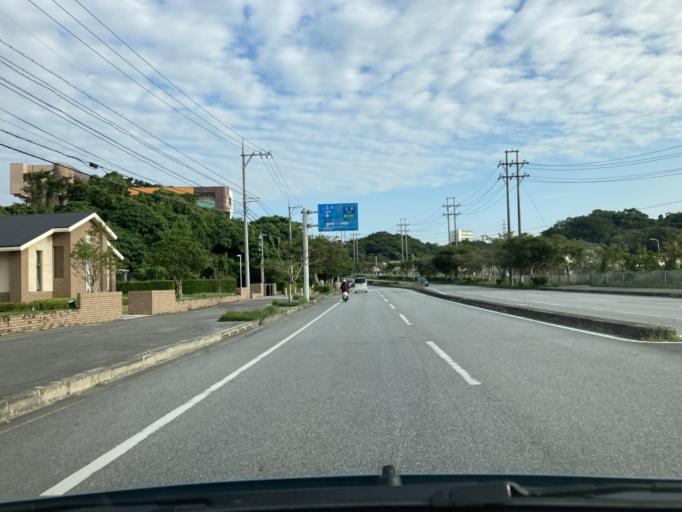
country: JP
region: Okinawa
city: Okinawa
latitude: 26.3579
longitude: 127.8015
